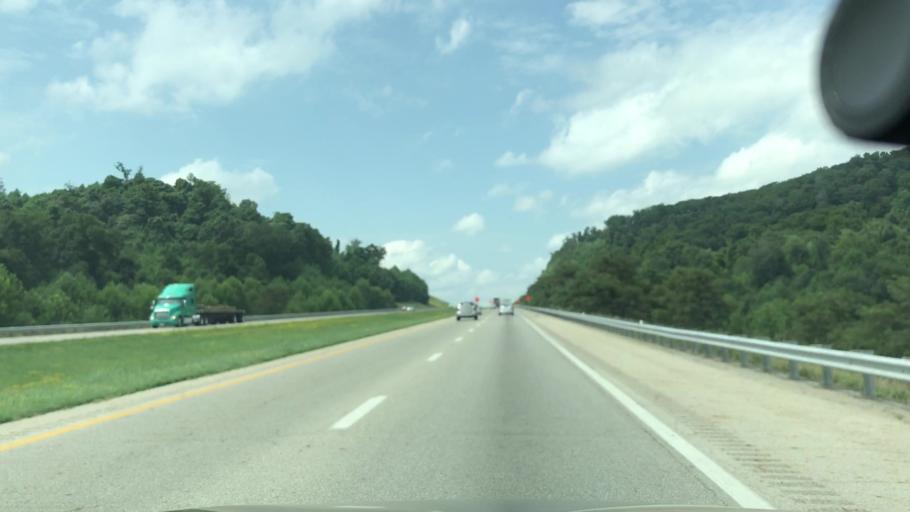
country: US
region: Ohio
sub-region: Pike County
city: Waverly
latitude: 39.2212
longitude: -82.8275
